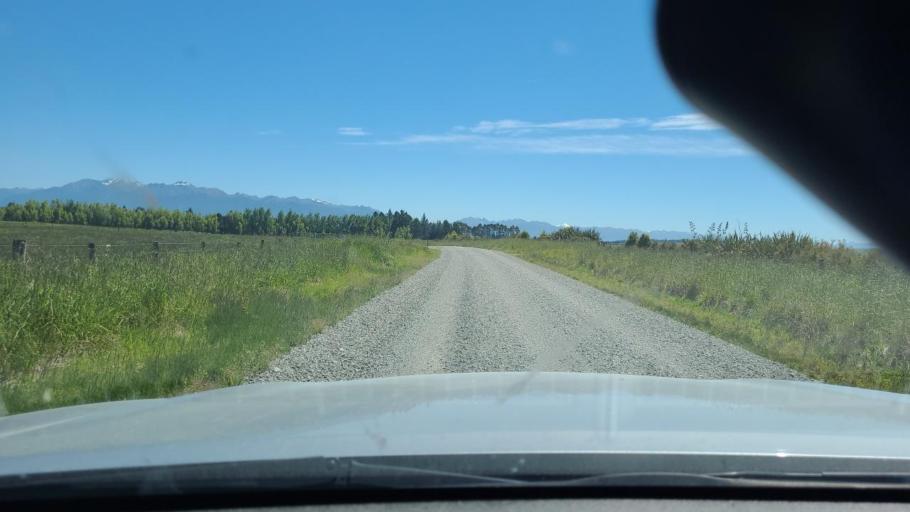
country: NZ
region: Southland
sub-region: Southland District
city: Te Anau
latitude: -45.4659
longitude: 167.8815
